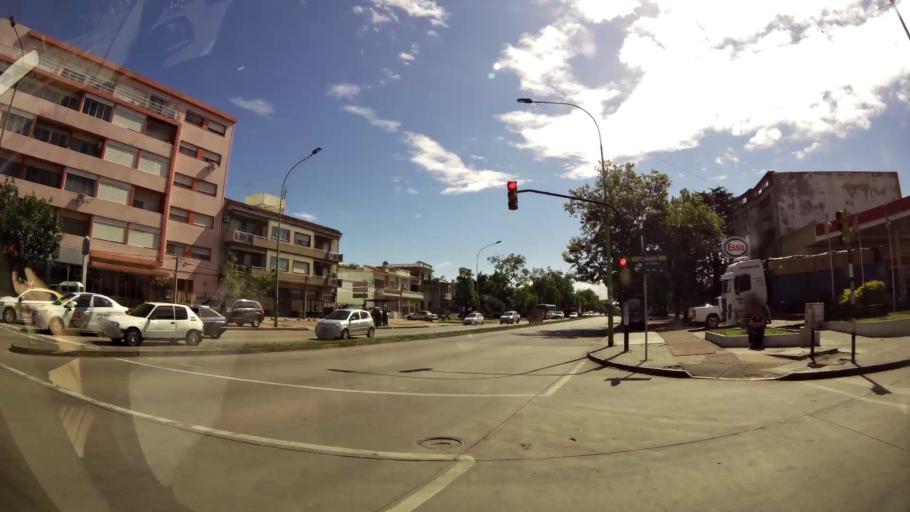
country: UY
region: Montevideo
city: Montevideo
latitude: -34.8714
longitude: -56.1903
